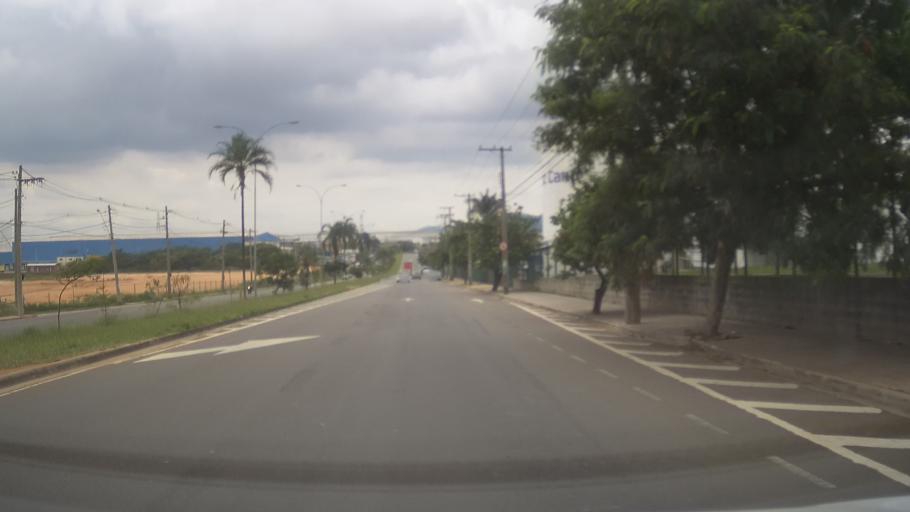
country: BR
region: Sao Paulo
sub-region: Itupeva
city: Itupeva
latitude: -23.1559
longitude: -47.0074
